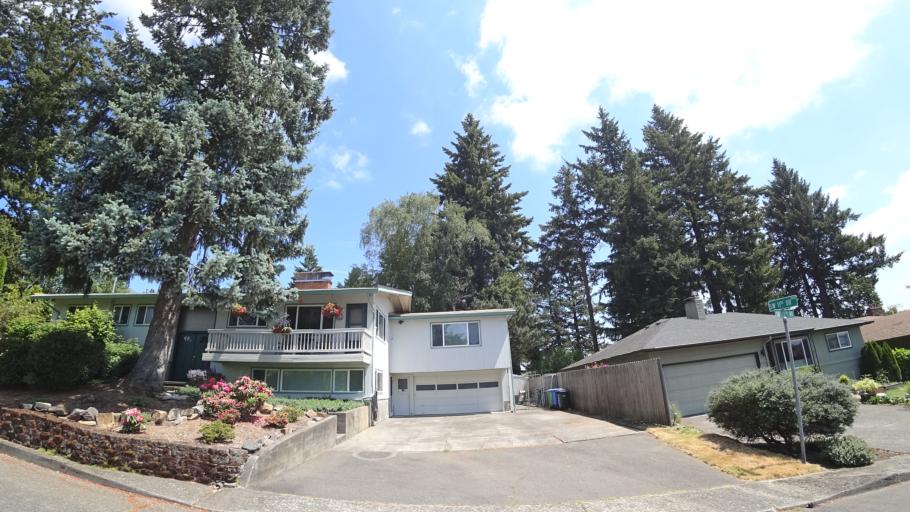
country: US
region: Oregon
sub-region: Multnomah County
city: Portland
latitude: 45.4737
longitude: -122.6886
